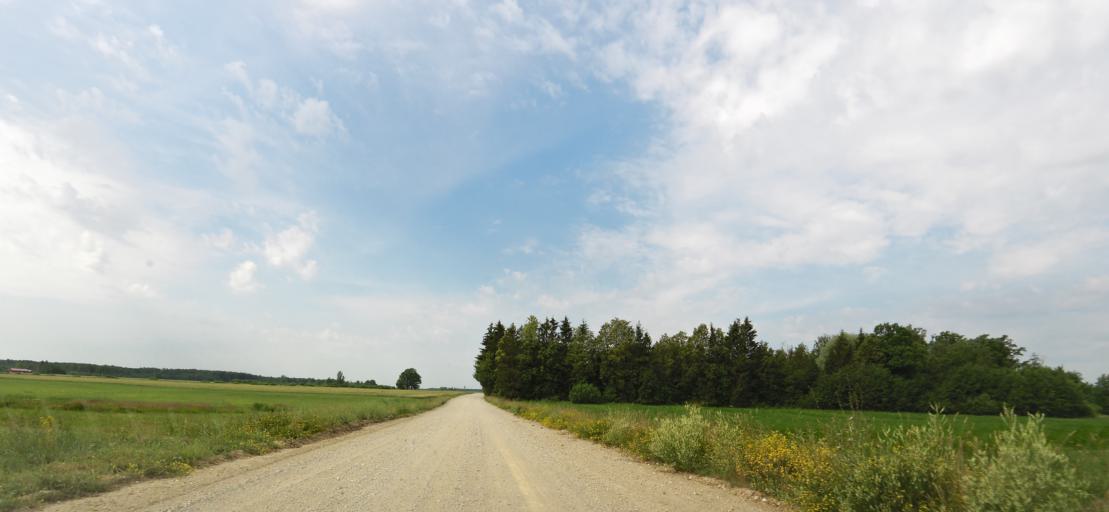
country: LT
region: Panevezys
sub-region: Birzai
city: Birzai
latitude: 56.2728
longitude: 24.5850
